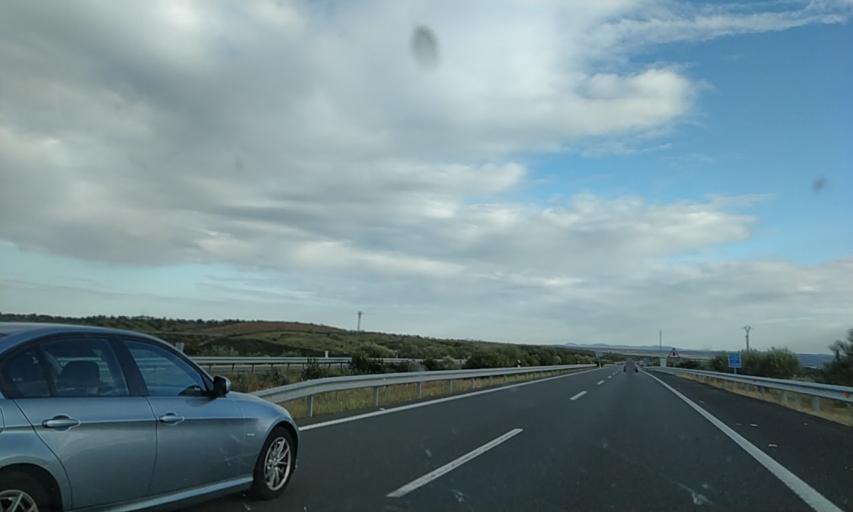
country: ES
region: Extremadura
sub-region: Provincia de Caceres
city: Canaveral
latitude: 39.7989
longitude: -6.3682
